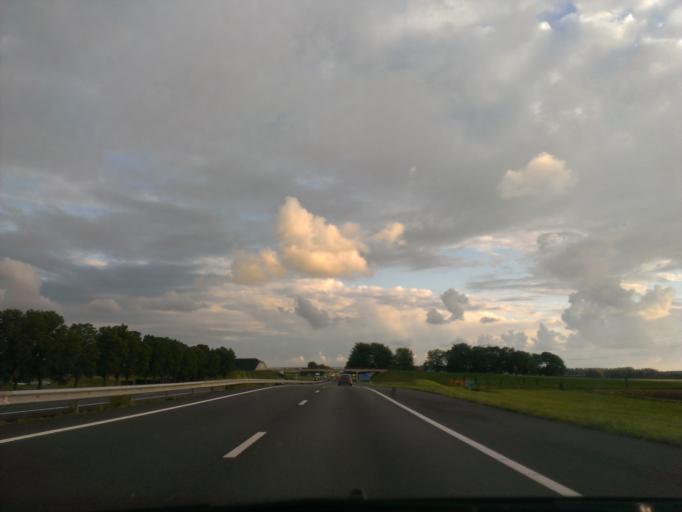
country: NL
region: South Holland
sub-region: Gemeente Oud-Beijerland
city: Oud-Beijerland
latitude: 51.7661
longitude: 4.4207
